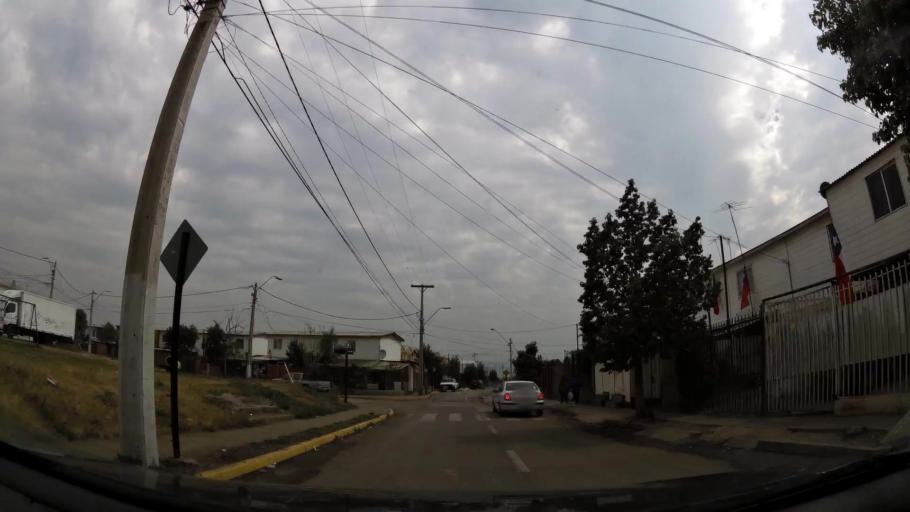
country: CL
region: Santiago Metropolitan
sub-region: Provincia de Chacabuco
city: Chicureo Abajo
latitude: -33.1850
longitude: -70.6646
